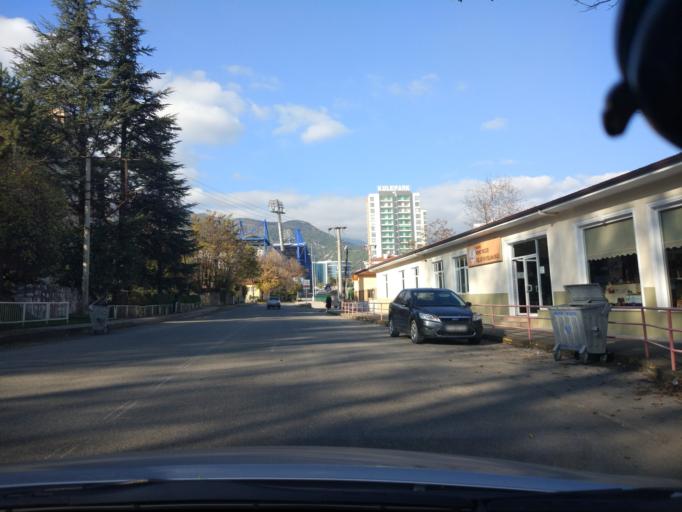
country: TR
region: Karabuk
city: Karabuk
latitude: 41.2022
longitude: 32.6222
